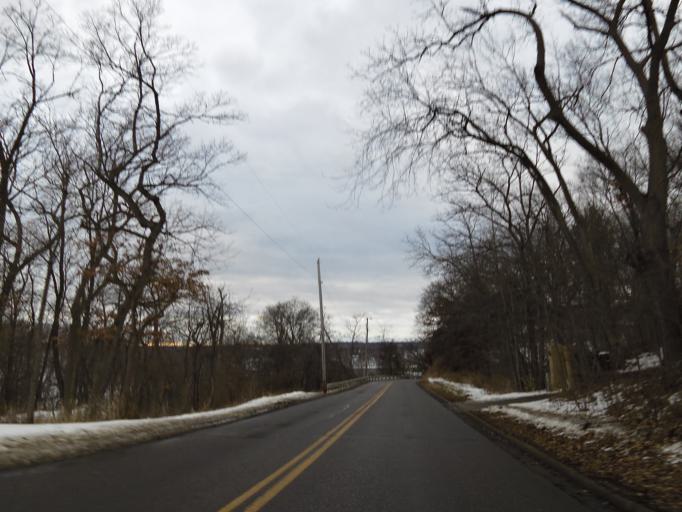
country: US
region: Wisconsin
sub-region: Saint Croix County
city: Hudson
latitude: 44.9705
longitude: -92.7529
